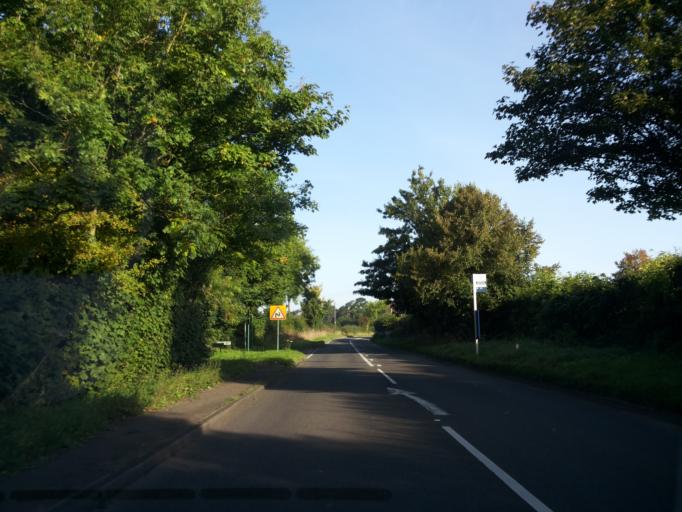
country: GB
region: England
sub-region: Solihull
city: Knowle
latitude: 52.3601
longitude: -1.7046
